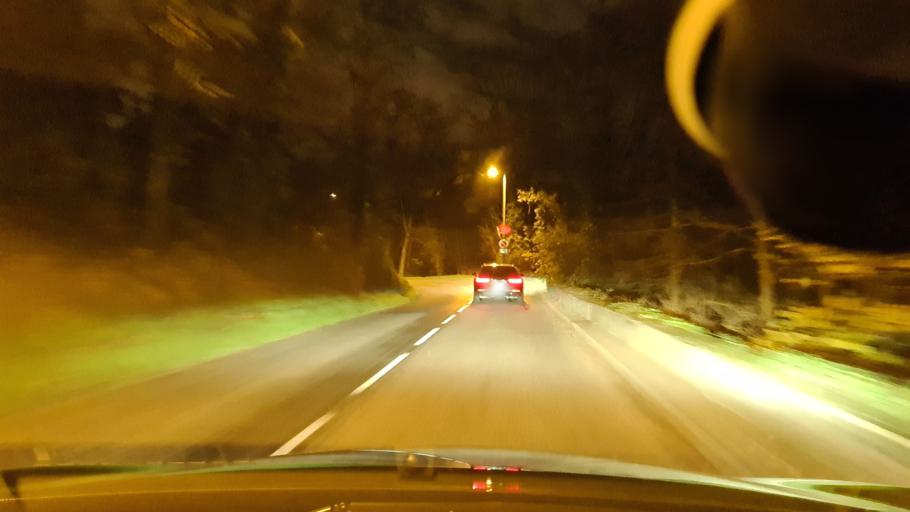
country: FR
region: Rhone-Alpes
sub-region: Departement du Rhone
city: Limonest
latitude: 45.8276
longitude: 4.7867
